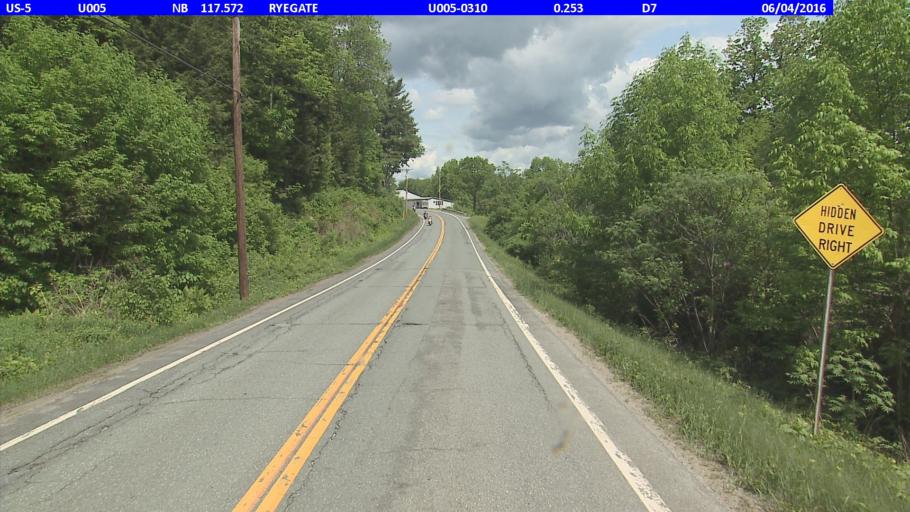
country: US
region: New Hampshire
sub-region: Grafton County
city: Woodsville
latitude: 44.1612
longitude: -72.0485
